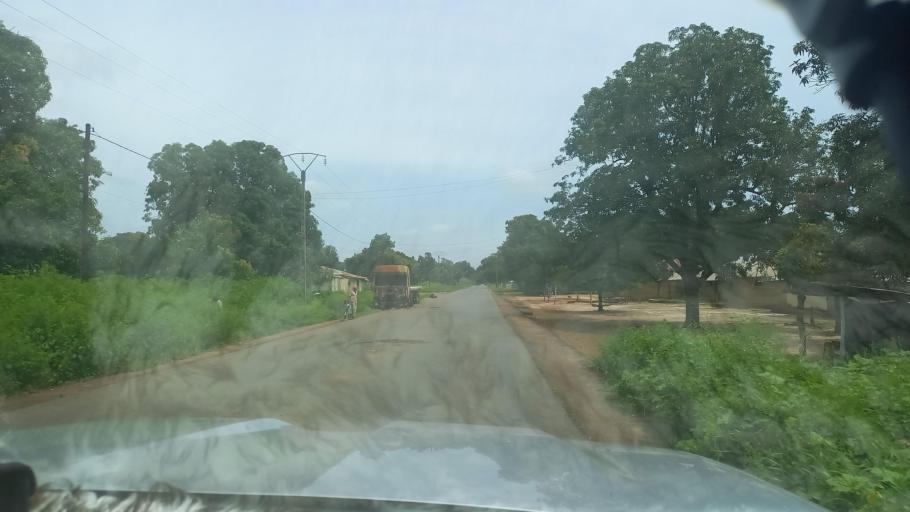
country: SN
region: Kolda
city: Marsassoum
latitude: 12.9640
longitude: -15.9748
